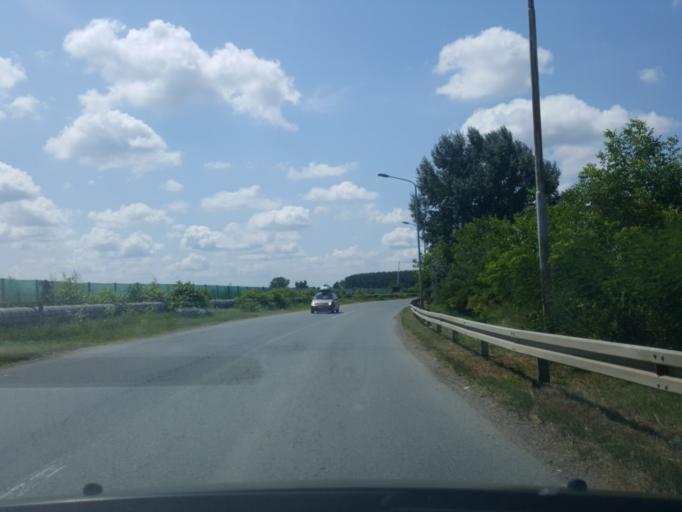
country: RS
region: Autonomna Pokrajina Vojvodina
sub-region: Sremski Okrug
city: Sremska Mitrovica
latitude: 44.9691
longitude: 19.6364
